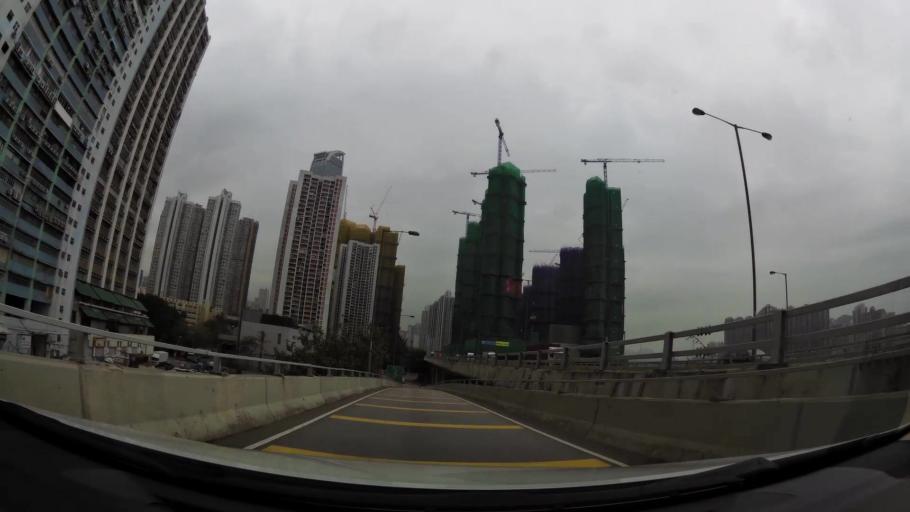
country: HK
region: Tsuen Wan
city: Tsuen Wan
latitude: 22.3721
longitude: 114.1072
